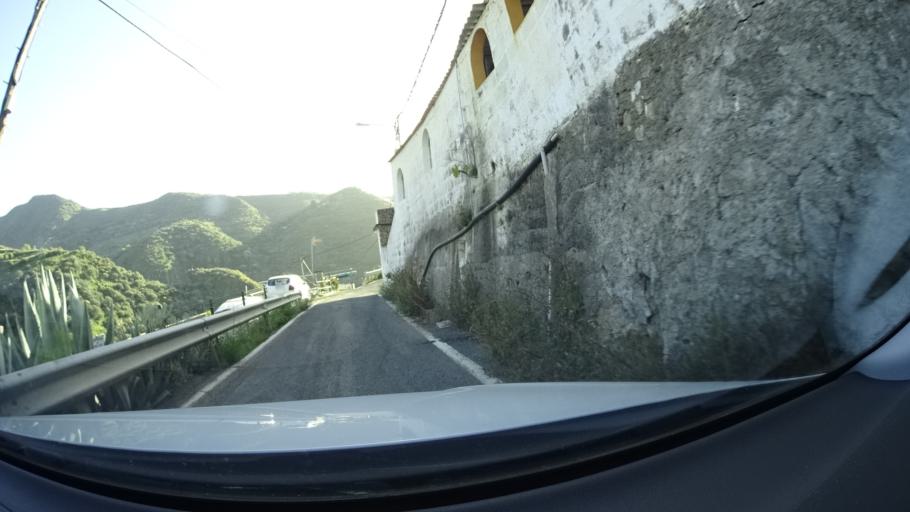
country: ES
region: Canary Islands
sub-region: Provincia de Las Palmas
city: Artenara
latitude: 28.0432
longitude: -15.6510
